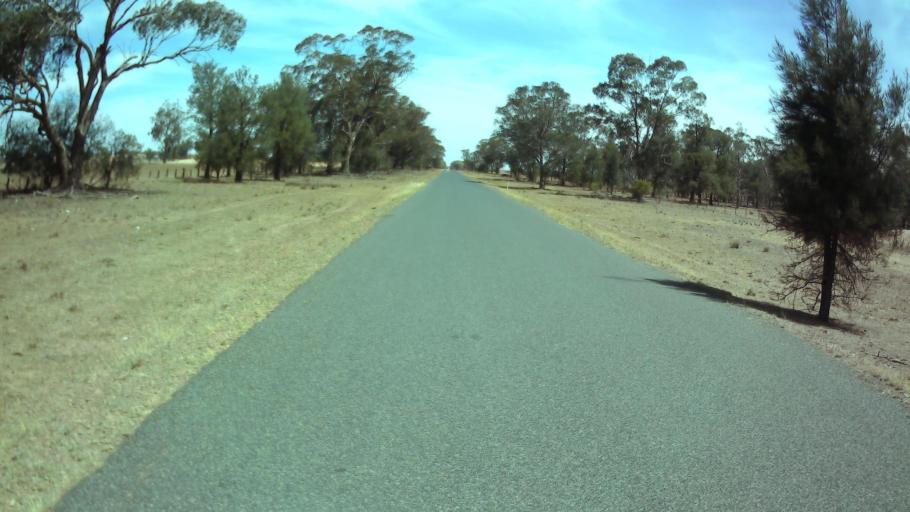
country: AU
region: New South Wales
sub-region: Weddin
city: Grenfell
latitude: -33.8641
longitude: 147.7460
